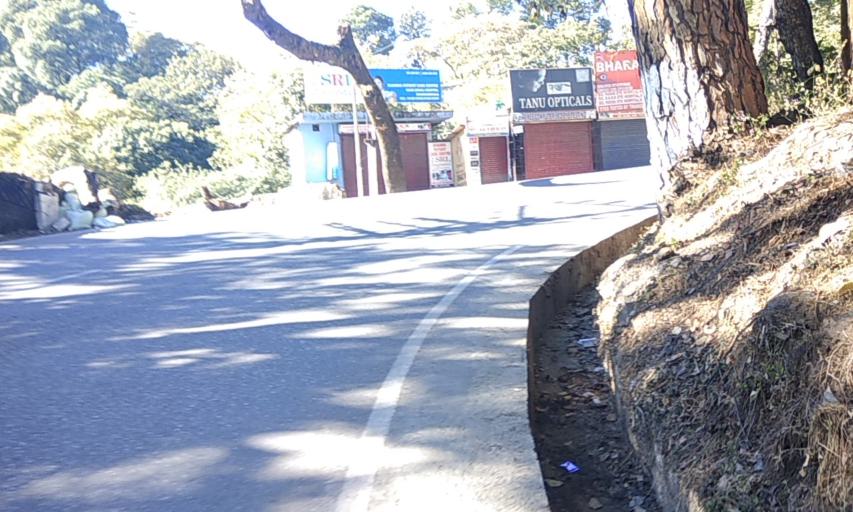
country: IN
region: Himachal Pradesh
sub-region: Kangra
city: Dharmsala
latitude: 32.2136
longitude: 76.3191
